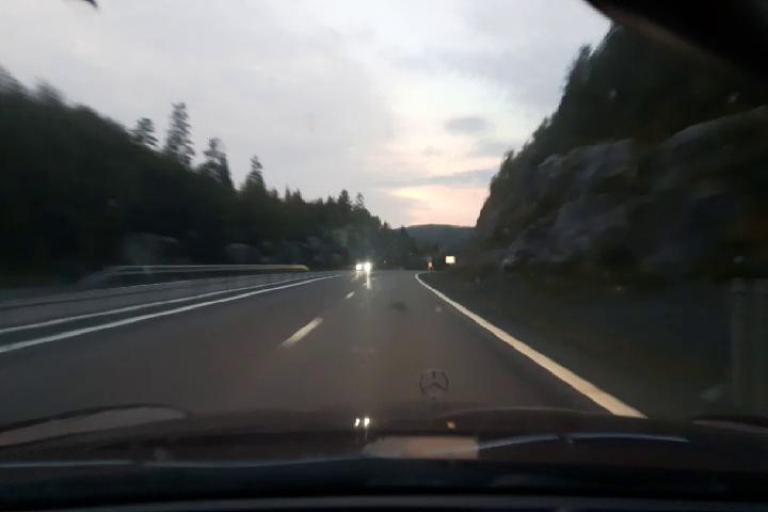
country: SE
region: Vaesternorrland
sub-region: Kramfors Kommun
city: Nordingra
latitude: 62.9485
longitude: 18.0937
